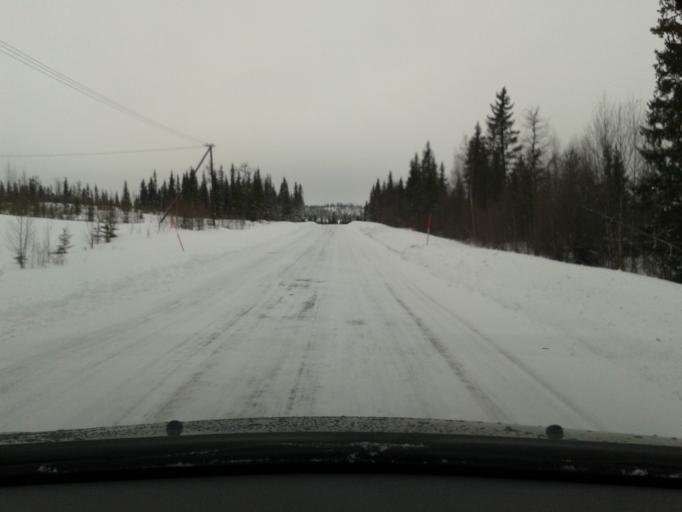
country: SE
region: Vaesterbotten
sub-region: Vilhelmina Kommun
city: Sjoberg
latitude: 65.2066
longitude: 15.9886
